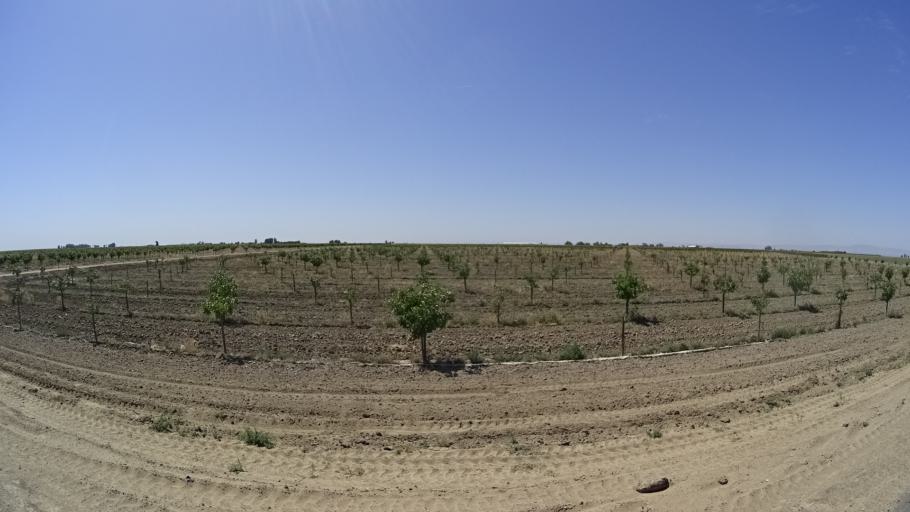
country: US
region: California
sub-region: Kings County
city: Stratford
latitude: 36.1895
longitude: -119.7899
